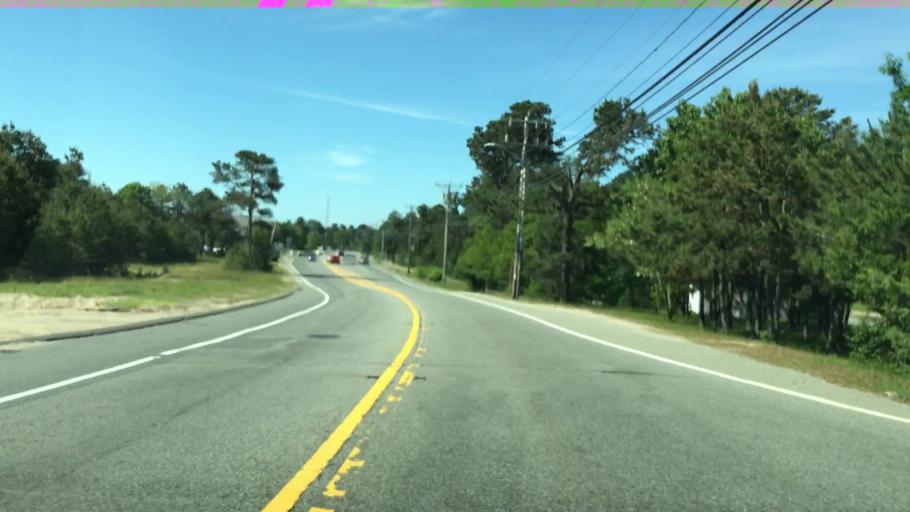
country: US
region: Massachusetts
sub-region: Barnstable County
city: Mashpee
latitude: 41.6156
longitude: -70.4892
